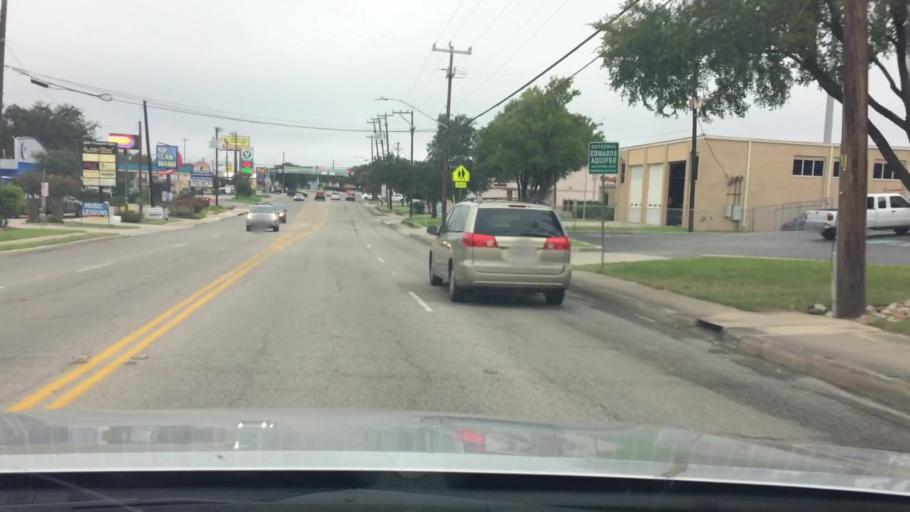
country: US
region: Texas
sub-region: Bexar County
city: Hollywood Park
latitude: 29.5848
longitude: -98.4496
